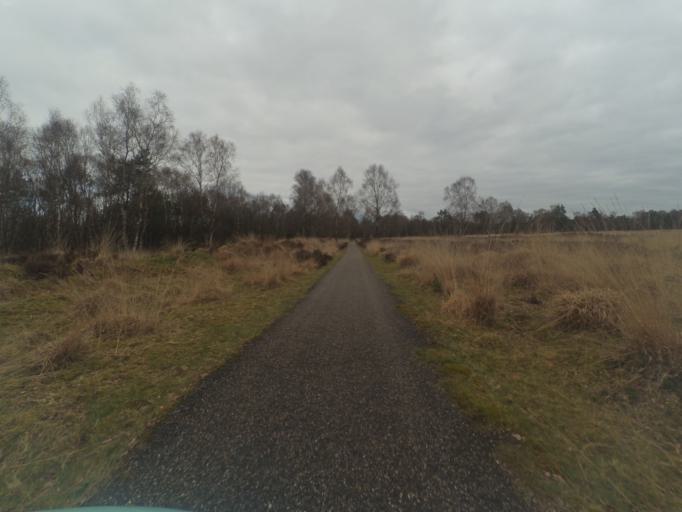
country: NL
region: Gelderland
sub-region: Gemeente Rozendaal
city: Rozendaal
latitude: 52.0369
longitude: 5.9384
